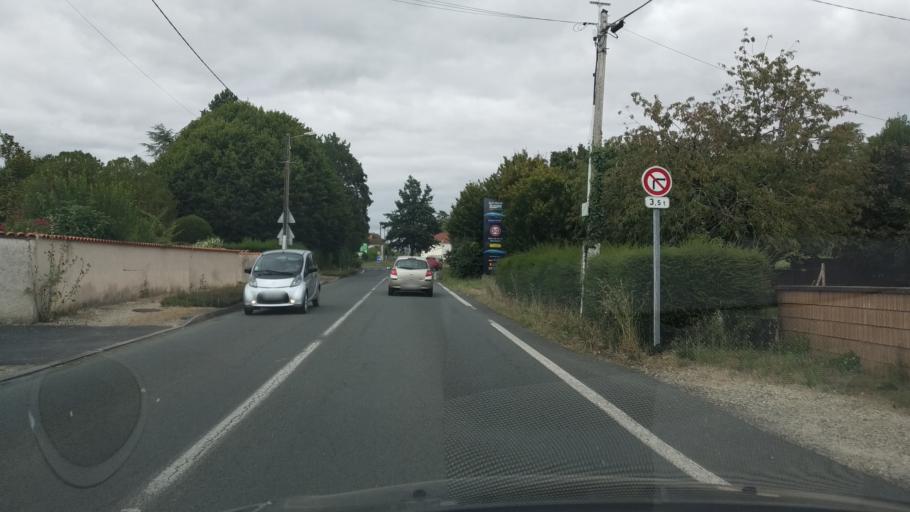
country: FR
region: Poitou-Charentes
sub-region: Departement de la Vienne
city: Saint-Benoit
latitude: 46.5581
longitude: 0.3551
